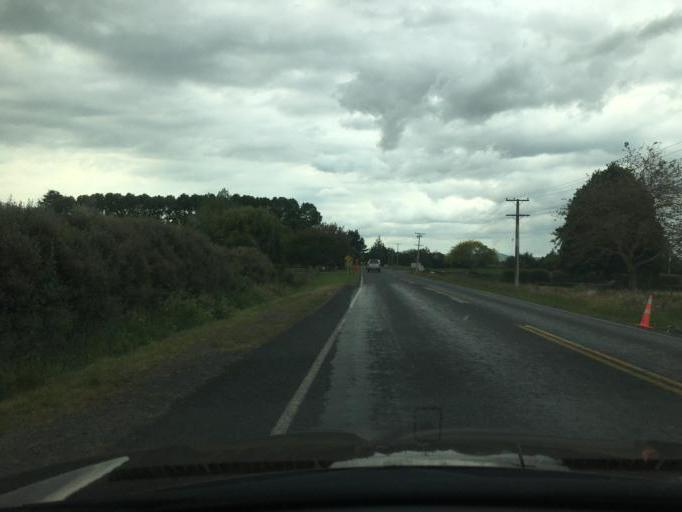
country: NZ
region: Waikato
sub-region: Waipa District
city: Cambridge
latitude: -37.9046
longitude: 175.4514
